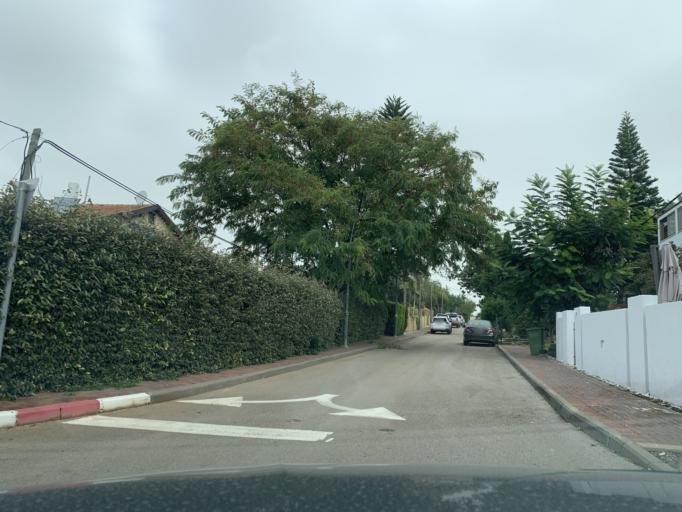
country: IL
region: Central District
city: Jaljulya
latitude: 32.1615
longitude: 34.9450
